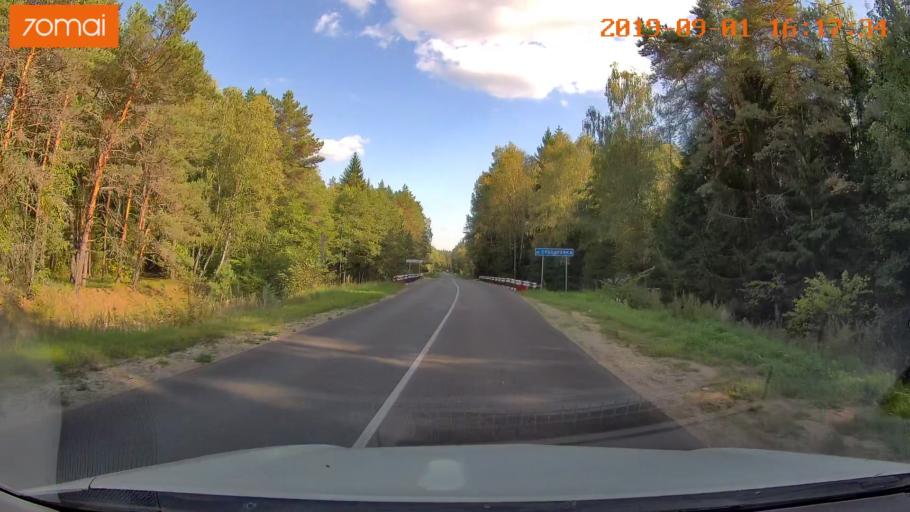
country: RU
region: Kaluga
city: Maloyaroslavets
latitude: 54.9075
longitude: 36.5086
